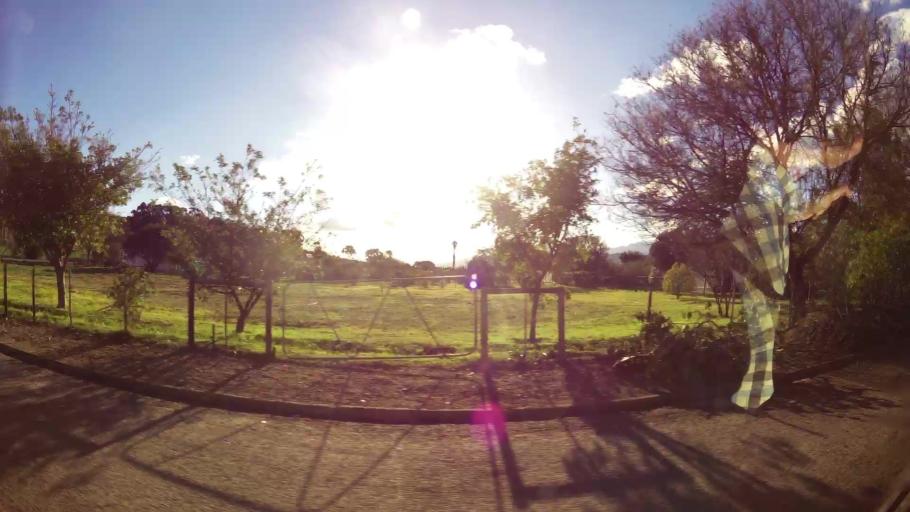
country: ZA
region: Western Cape
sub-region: Eden District Municipality
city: Riversdale
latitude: -34.0974
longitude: 20.9566
